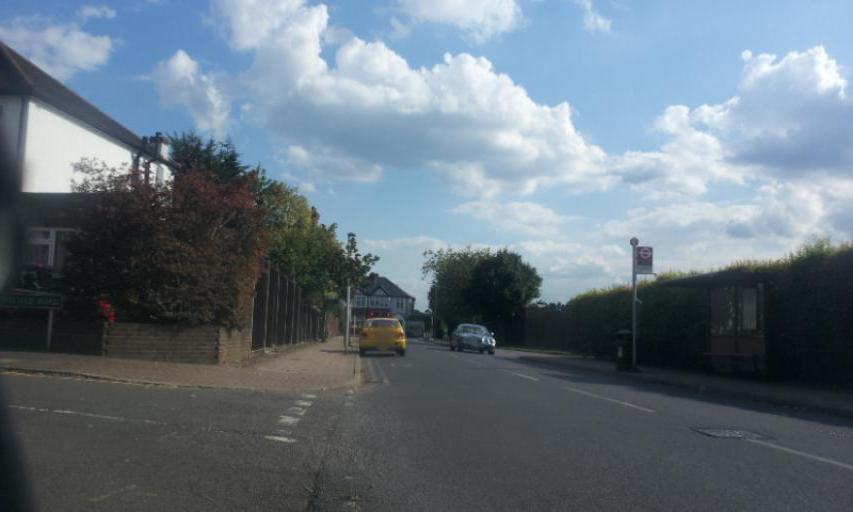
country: GB
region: England
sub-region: Greater London
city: Bromley
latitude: 51.3994
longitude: 0.0369
